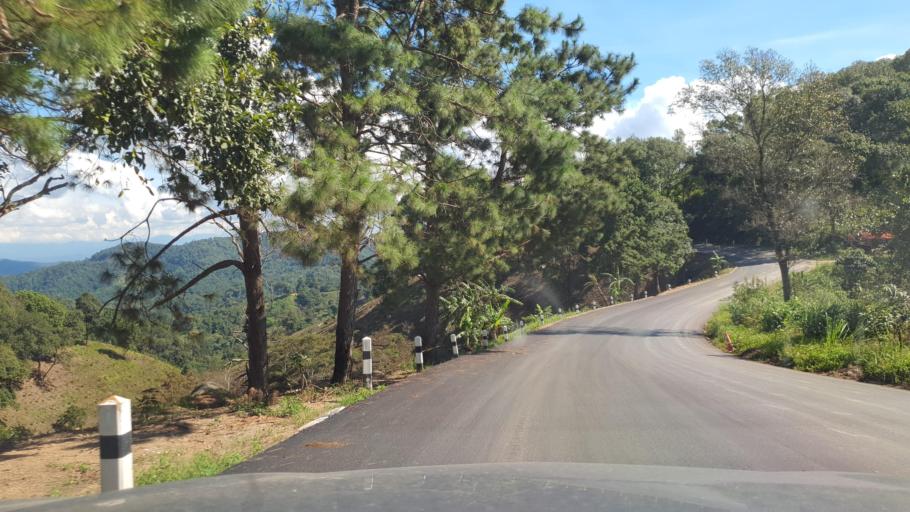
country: TH
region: Chiang Mai
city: Phrao
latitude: 19.3187
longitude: 99.3277
